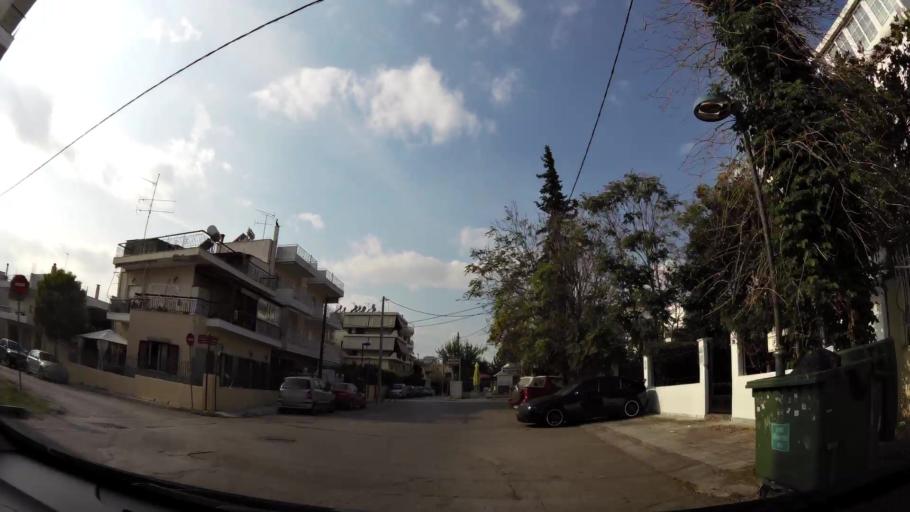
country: GR
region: Attica
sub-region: Nomarchia Athinas
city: Irakleio
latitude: 38.0569
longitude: 23.7493
